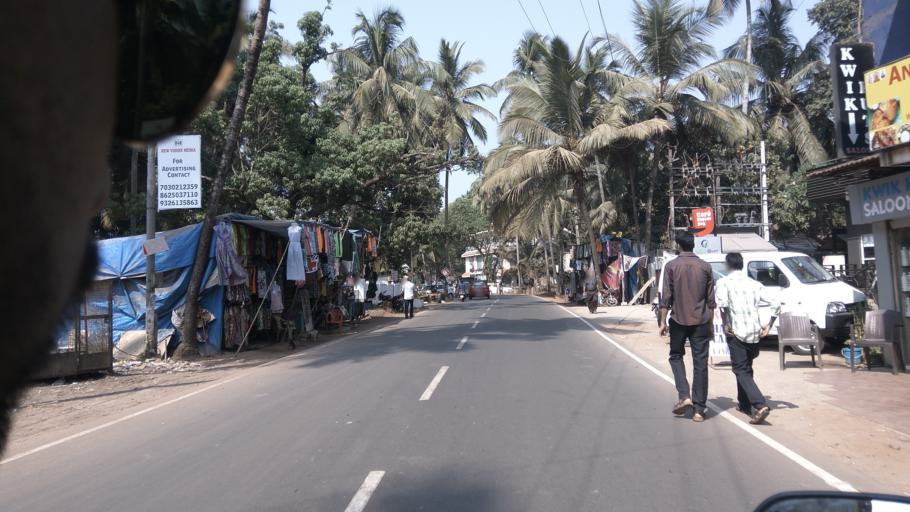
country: IN
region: Goa
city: Calangute
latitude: 15.5401
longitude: 73.7647
